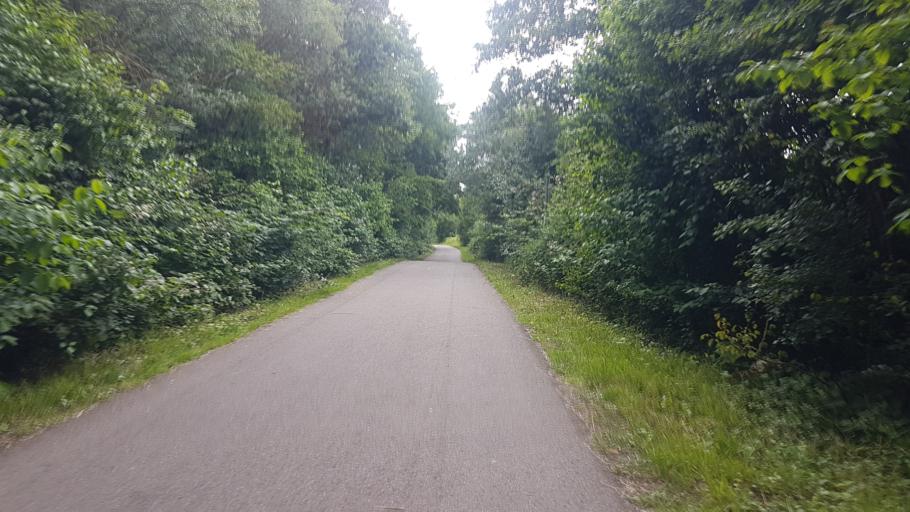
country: DE
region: Saarland
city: Bous
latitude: 49.2727
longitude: 6.7958
